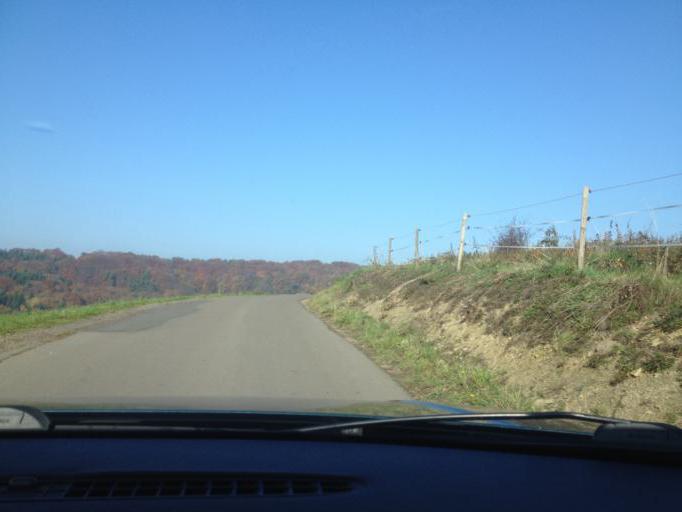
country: DE
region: Saarland
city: Sankt Wendel
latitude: 49.5024
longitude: 7.2057
